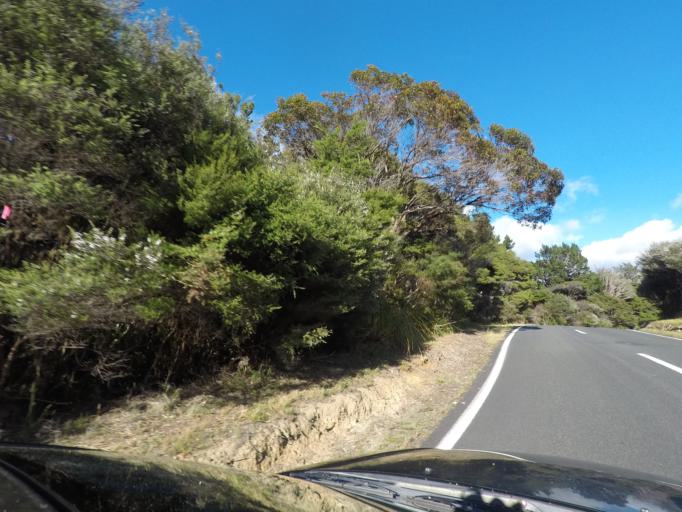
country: NZ
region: Auckland
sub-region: Auckland
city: Titirangi
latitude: -37.0041
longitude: 174.5983
